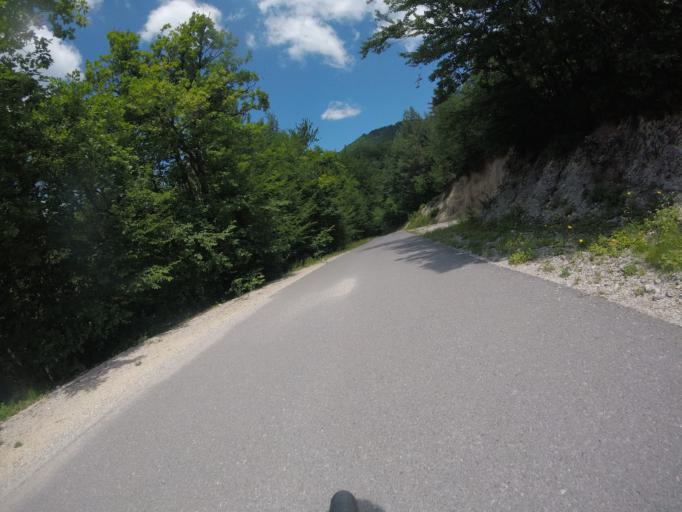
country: SI
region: Kostanjevica na Krki
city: Kostanjevica na Krki
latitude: 45.7648
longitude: 15.4076
